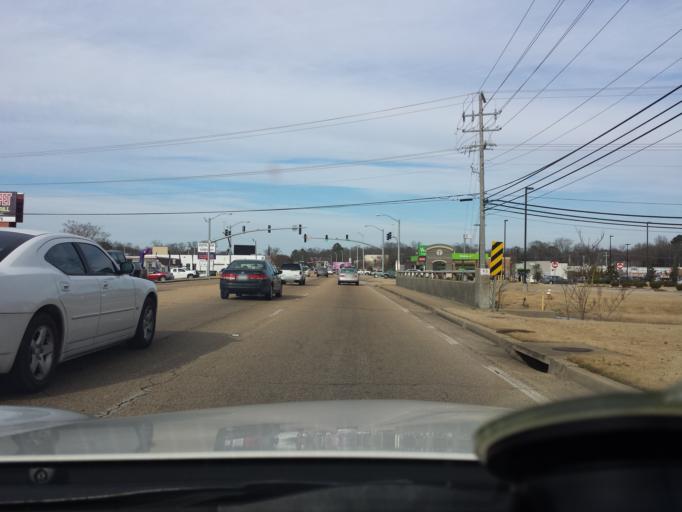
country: US
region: Mississippi
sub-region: Lee County
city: Tupelo
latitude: 34.2534
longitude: -88.7159
